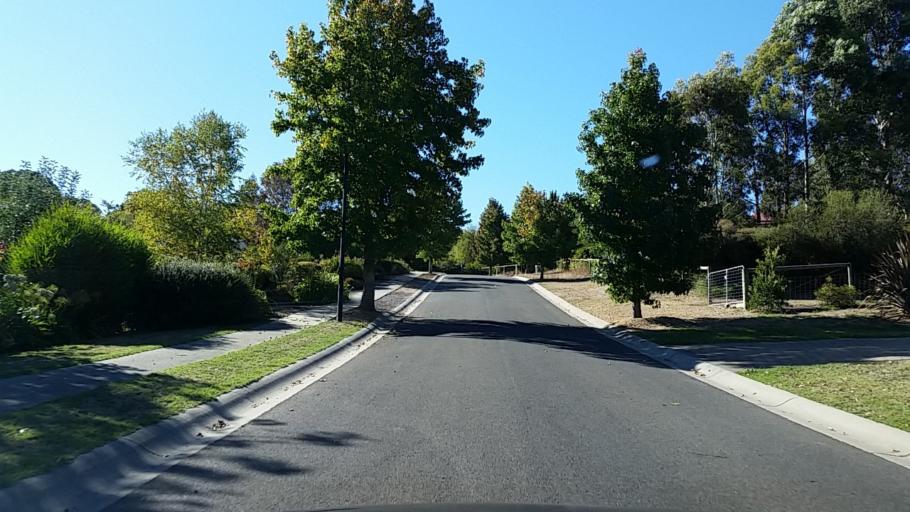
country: AU
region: South Australia
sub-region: Mount Barker
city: Mount Barker
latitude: -35.0619
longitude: 138.8843
